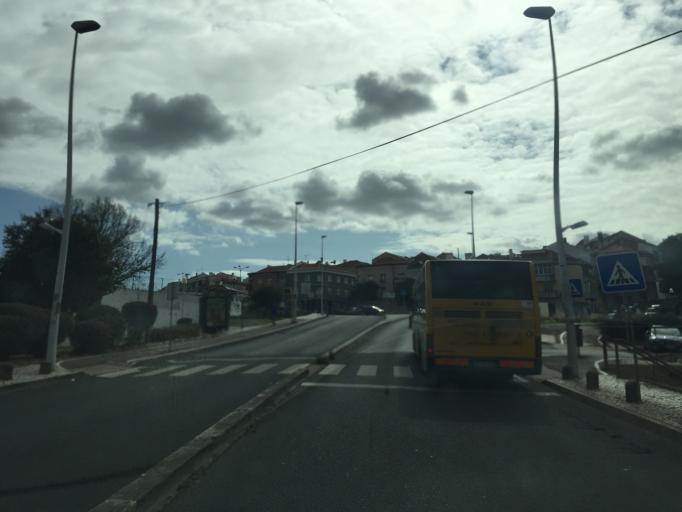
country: PT
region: Lisbon
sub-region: Odivelas
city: Pontinha
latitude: 38.7442
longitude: -9.2054
